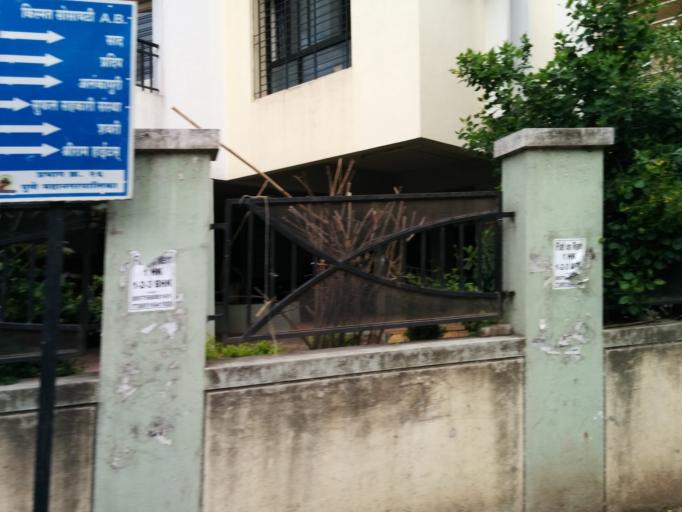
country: IN
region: Maharashtra
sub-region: Pune Division
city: Pune
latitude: 18.5129
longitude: 73.8155
